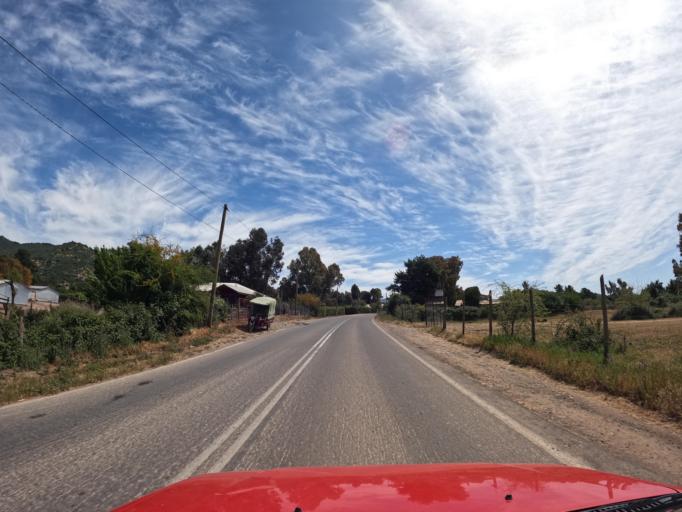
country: CL
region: Maule
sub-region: Provincia de Talca
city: Talca
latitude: -35.1224
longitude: -71.6733
